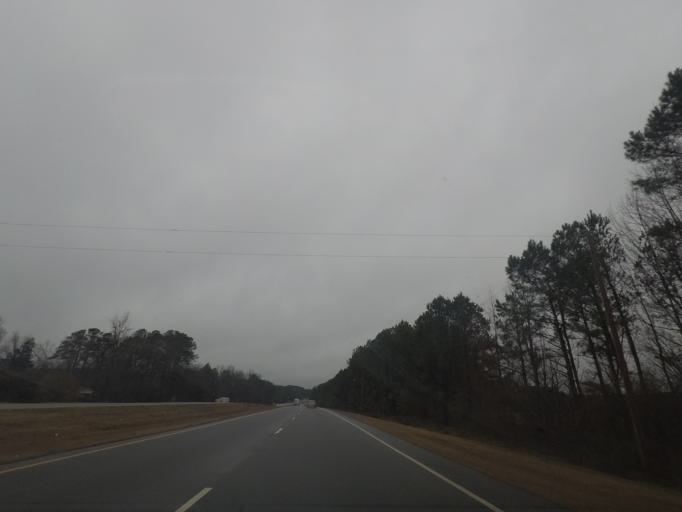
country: US
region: North Carolina
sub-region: Lee County
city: Broadway
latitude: 35.3213
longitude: -79.0912
